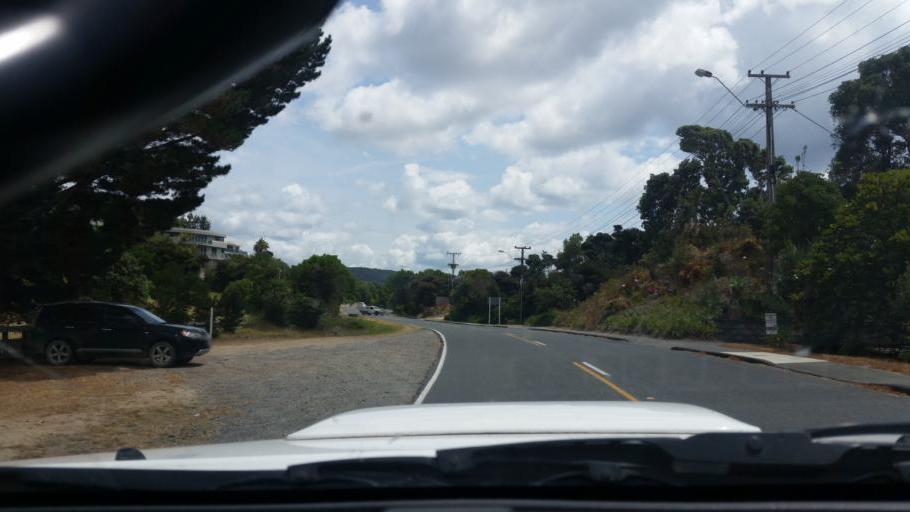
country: NZ
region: Auckland
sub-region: Auckland
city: Wellsford
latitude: -36.0946
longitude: 174.5858
